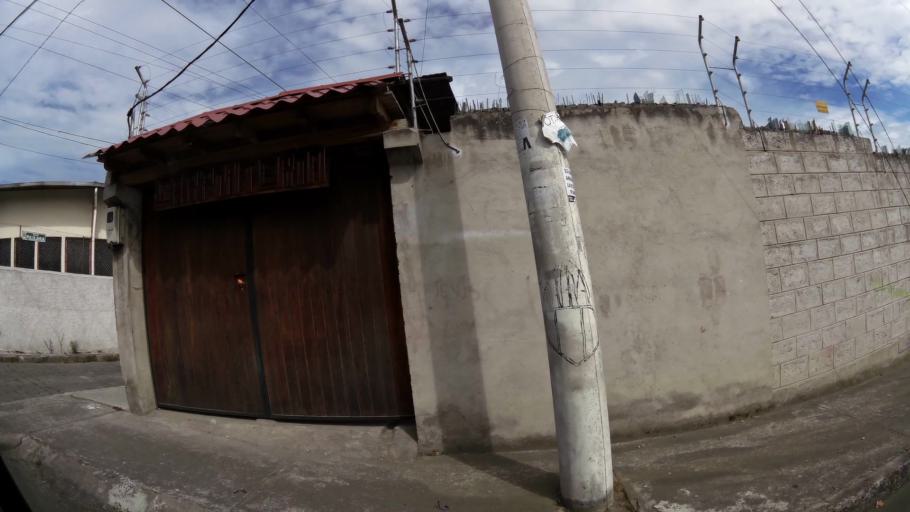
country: EC
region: Tungurahua
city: Ambato
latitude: -1.2437
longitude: -78.6237
